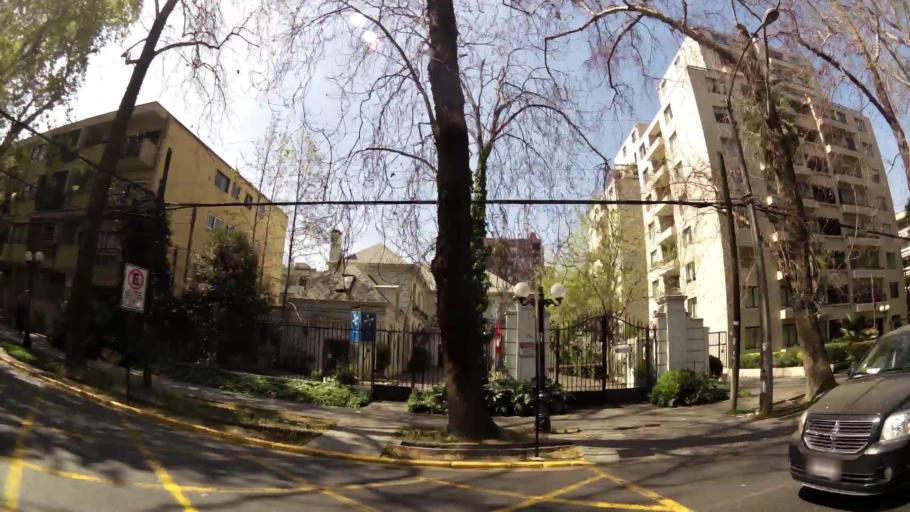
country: CL
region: Santiago Metropolitan
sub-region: Provincia de Santiago
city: Villa Presidente Frei, Nunoa, Santiago, Chile
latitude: -33.4252
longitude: -70.6086
